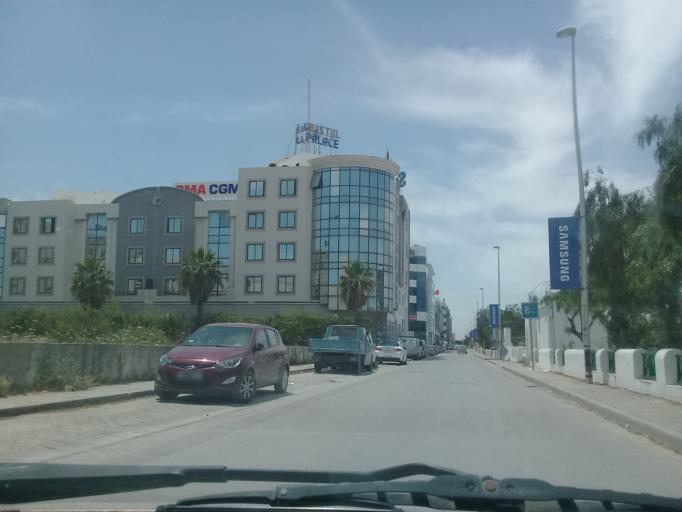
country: TN
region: Ariana
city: Ariana
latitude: 36.8374
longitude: 10.2336
